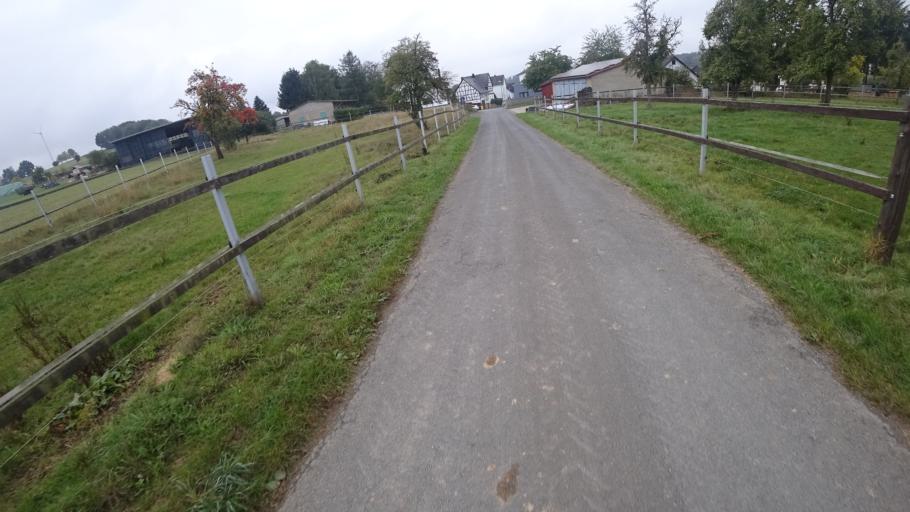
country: DE
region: Rheinland-Pfalz
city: Eppenrod
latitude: 50.4034
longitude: 7.9331
